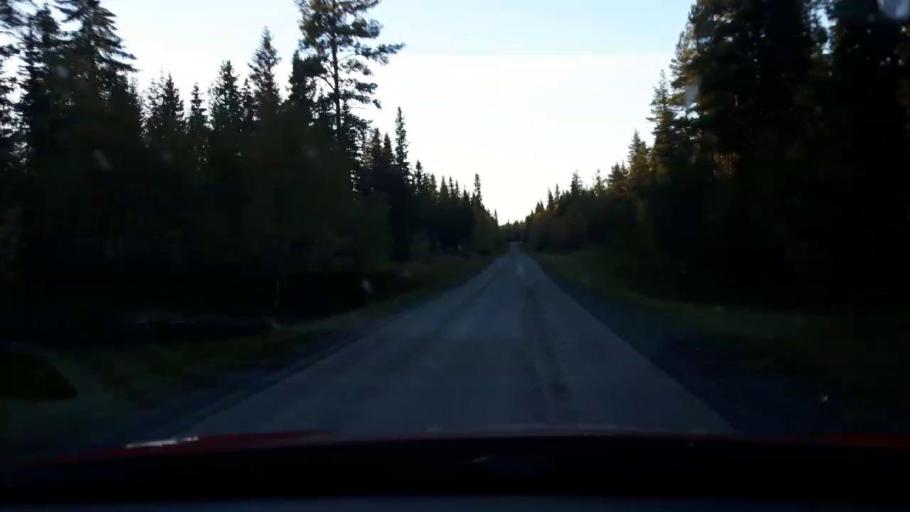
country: SE
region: Jaemtland
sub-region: Krokoms Kommun
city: Krokom
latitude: 63.4651
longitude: 14.3608
